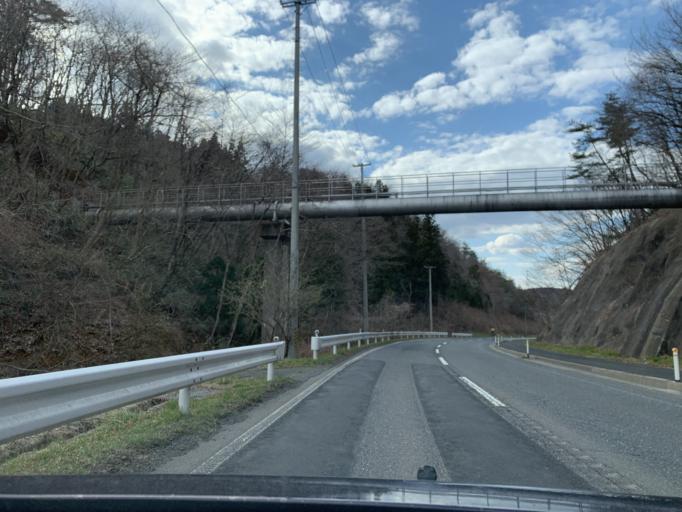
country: JP
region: Iwate
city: Ichinoseki
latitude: 38.8953
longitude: 141.2290
